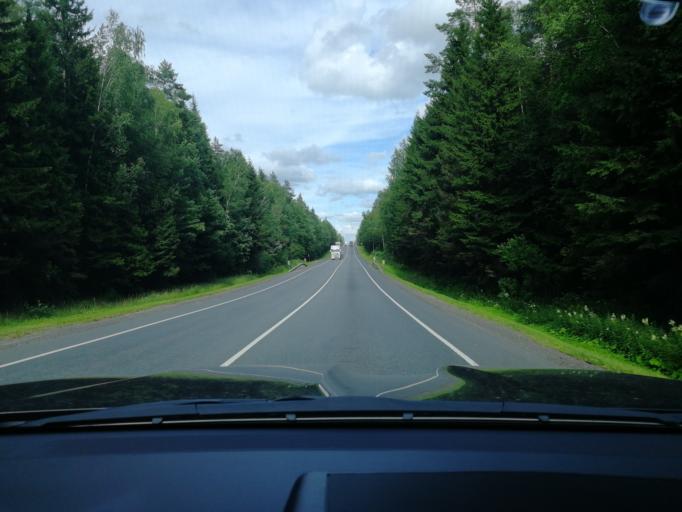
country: RU
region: Moskovskaya
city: Popovo
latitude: 55.0438
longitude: 37.7096
